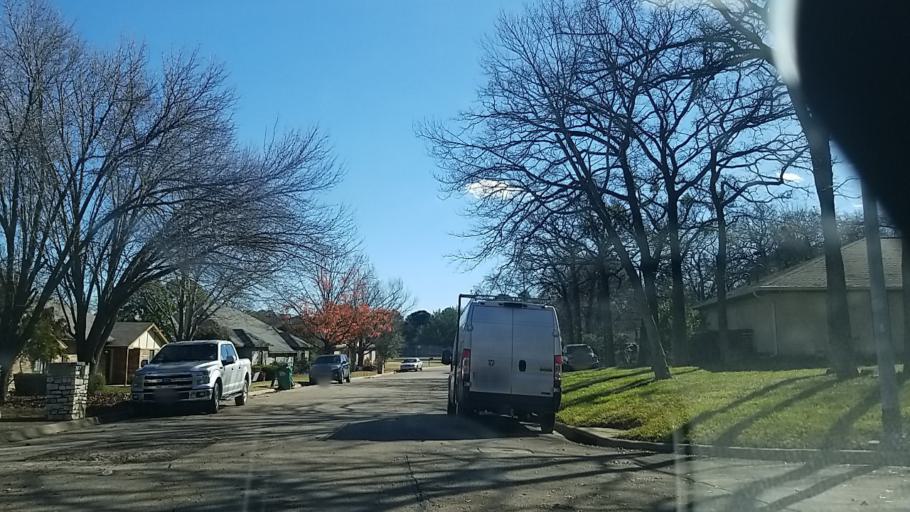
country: US
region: Texas
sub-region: Denton County
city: Denton
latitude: 33.1901
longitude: -97.1162
